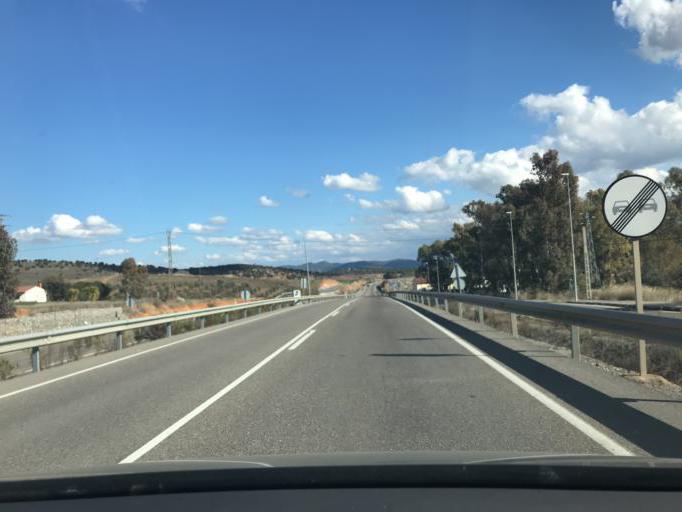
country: ES
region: Andalusia
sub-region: Province of Cordoba
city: Penarroya-Pueblonuevo
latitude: 38.2974
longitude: -5.2465
